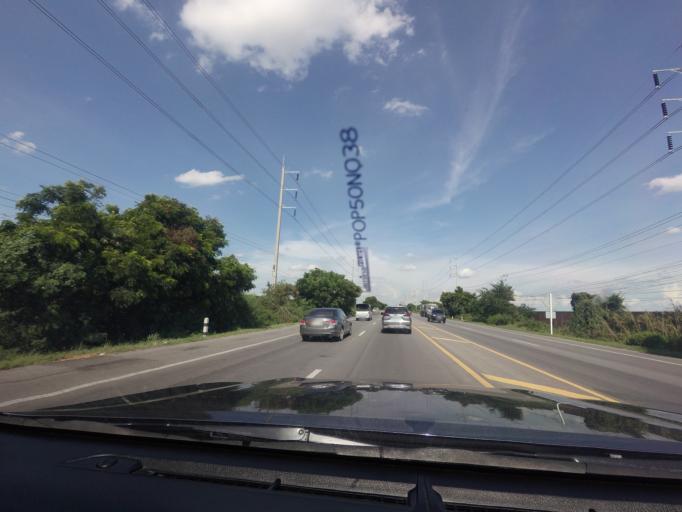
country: TH
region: Suphan Buri
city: Song Phi Nong
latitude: 14.1580
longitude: 100.1336
